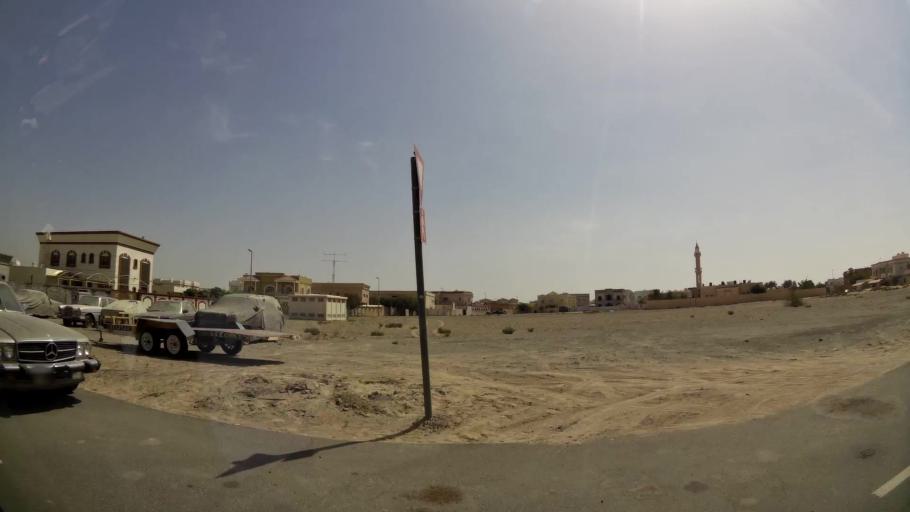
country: AE
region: Ash Shariqah
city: Sharjah
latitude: 25.2019
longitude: 55.4262
